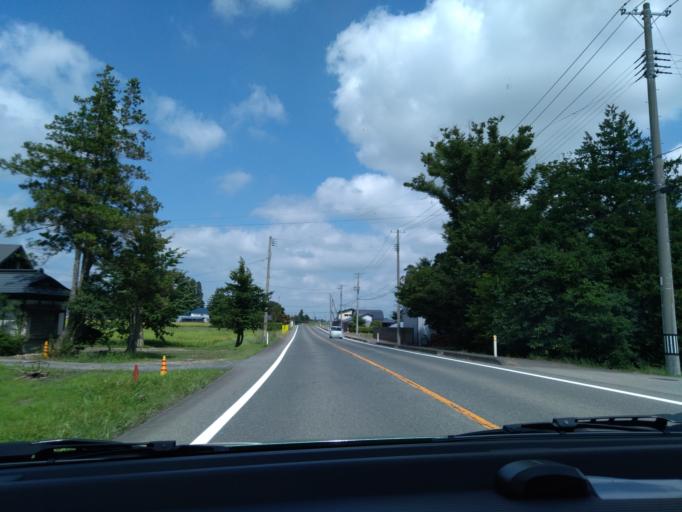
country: JP
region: Iwate
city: Hanamaki
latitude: 39.4314
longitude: 141.0926
